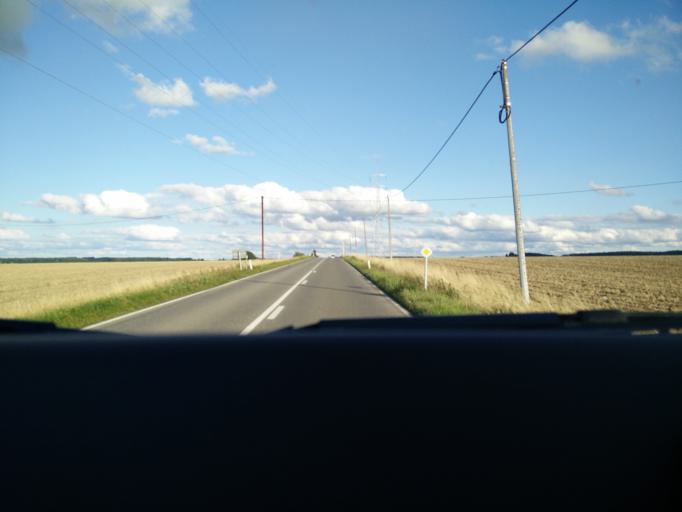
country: BE
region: Wallonia
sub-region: Province de Namur
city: Walcourt
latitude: 50.2218
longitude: 4.4293
